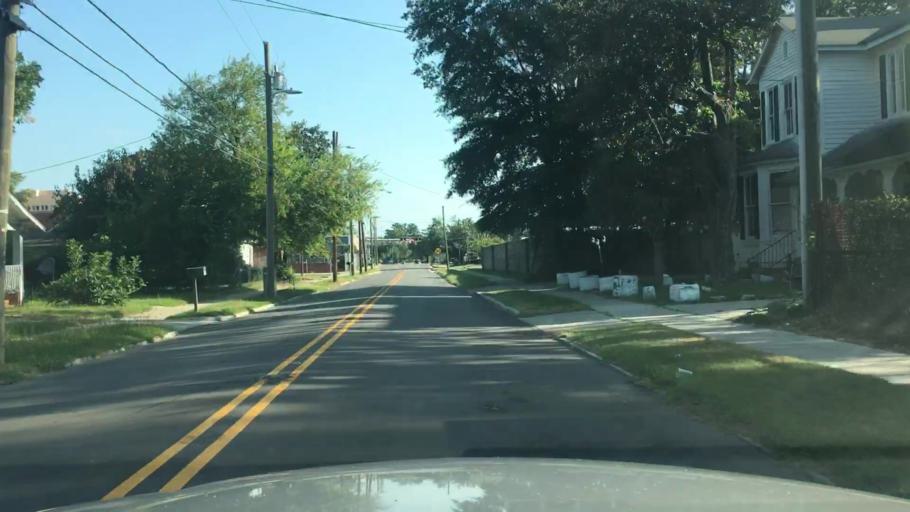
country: US
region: North Carolina
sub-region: Cumberland County
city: Fayetteville
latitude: 35.0473
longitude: -78.8764
